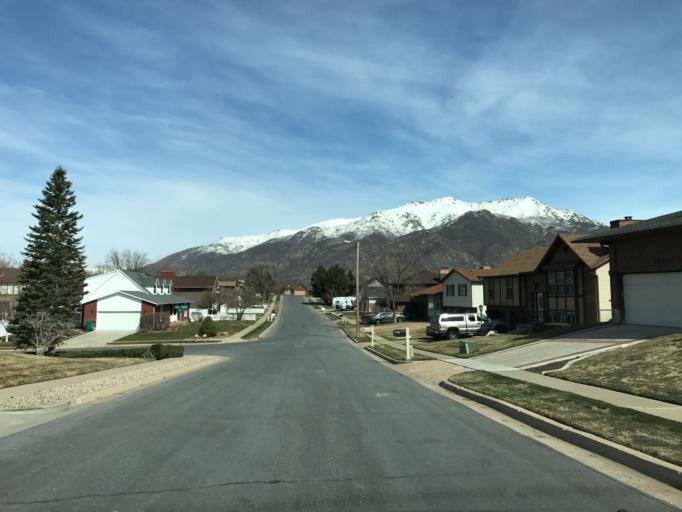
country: US
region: Utah
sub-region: Davis County
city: South Weber
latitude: 41.1108
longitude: -111.9117
